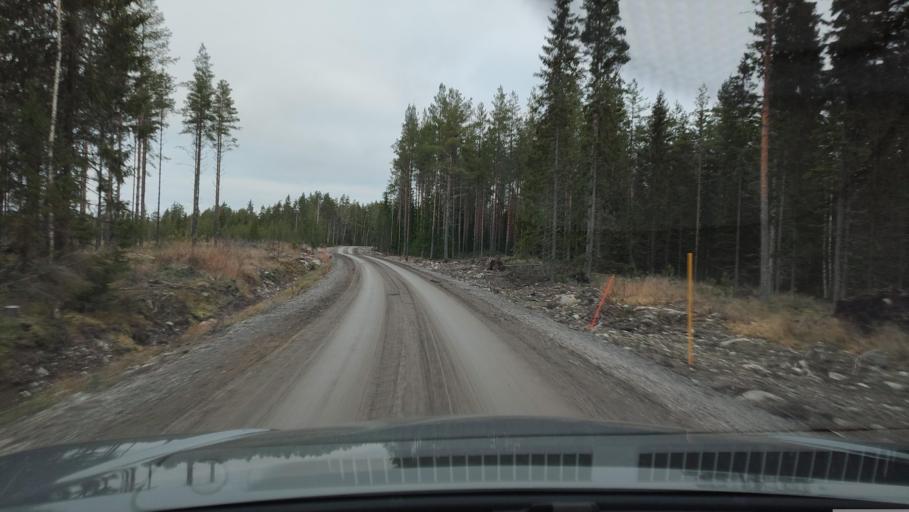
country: FI
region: Southern Ostrobothnia
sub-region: Suupohja
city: Karijoki
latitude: 62.1901
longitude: 21.5891
